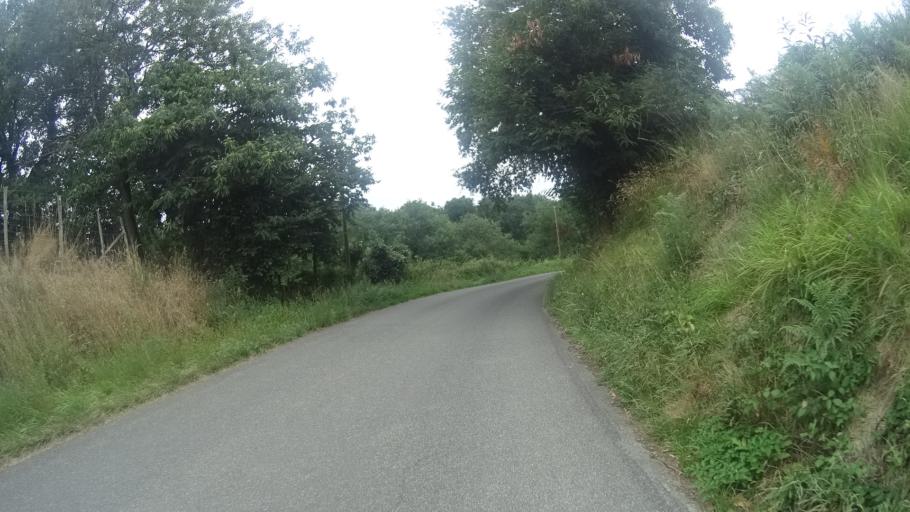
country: FR
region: Aquitaine
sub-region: Departement des Pyrenees-Atlantiques
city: Orthez
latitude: 43.4774
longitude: -0.7050
